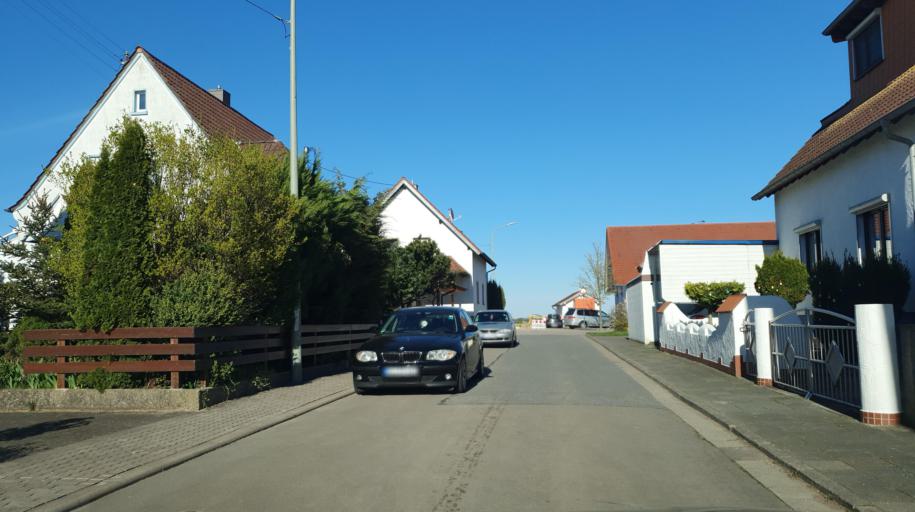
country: DE
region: Rheinland-Pfalz
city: Bruchmuhlbach-Miesau
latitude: 49.4011
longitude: 7.4386
